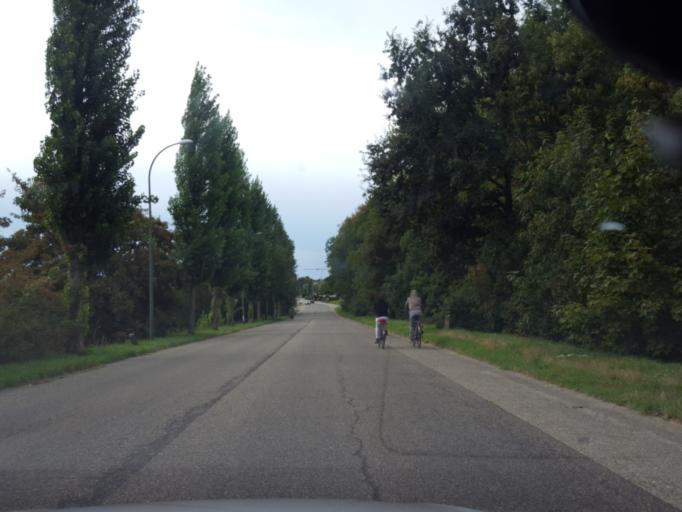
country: BE
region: Flanders
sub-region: Provincie Limburg
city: Maasmechelen
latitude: 50.9216
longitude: 5.7031
